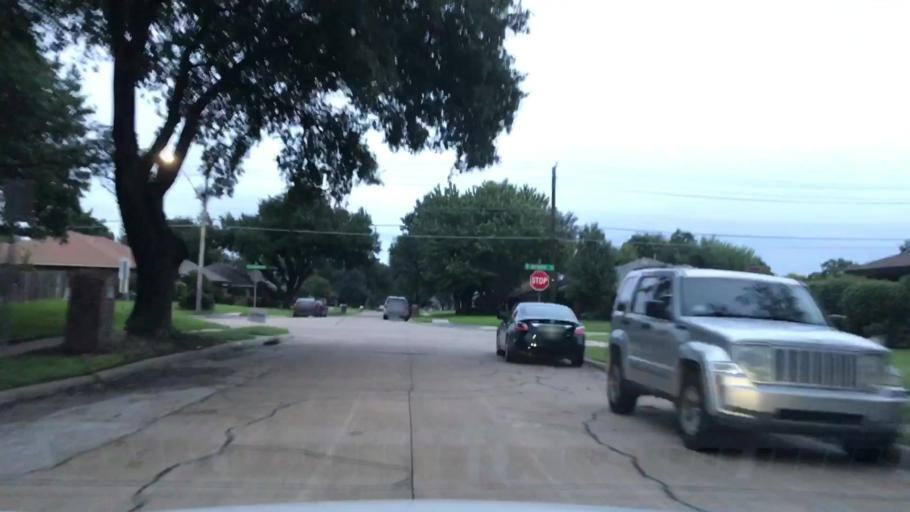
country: US
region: Texas
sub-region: Dallas County
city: Garland
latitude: 32.8494
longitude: -96.6213
